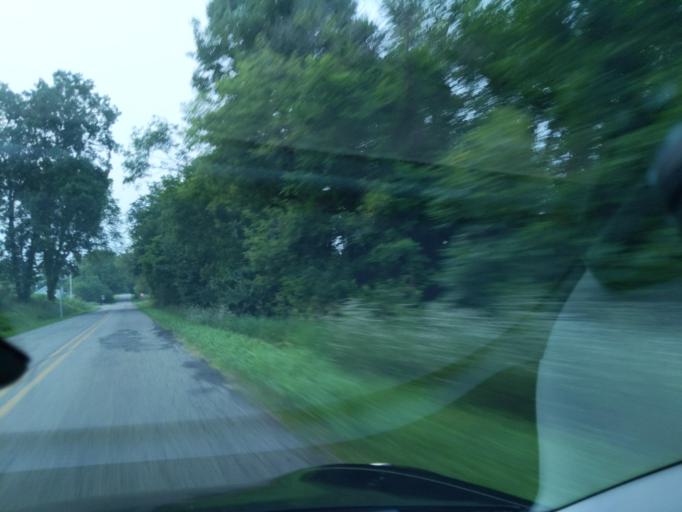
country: US
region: Michigan
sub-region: Ingham County
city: Leslie
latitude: 42.3698
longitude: -84.4924
